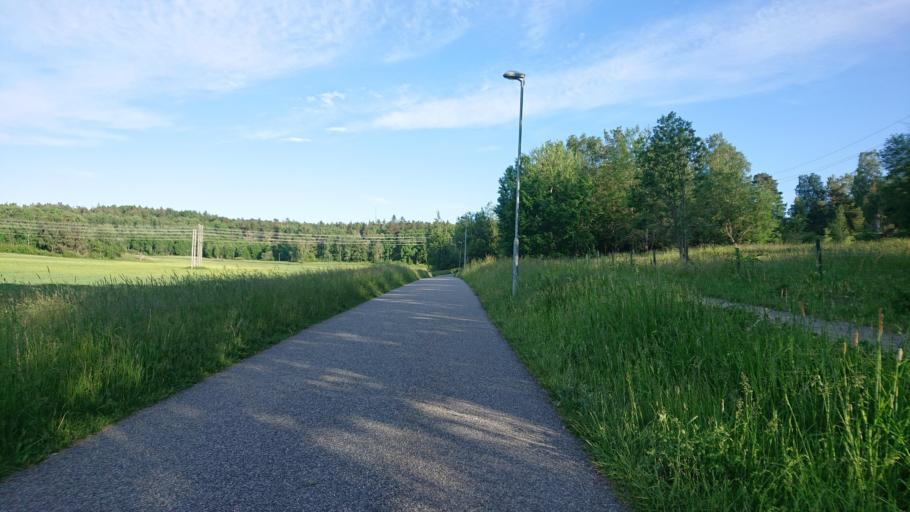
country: SE
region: Stockholm
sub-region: Osterakers Kommun
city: Akersberga
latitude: 59.4963
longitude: 18.3010
